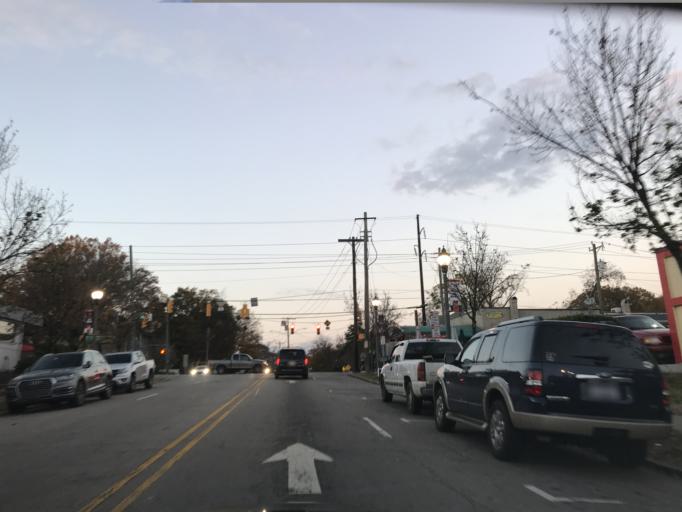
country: US
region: North Carolina
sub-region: Wake County
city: West Raleigh
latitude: 35.7881
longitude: -78.6472
